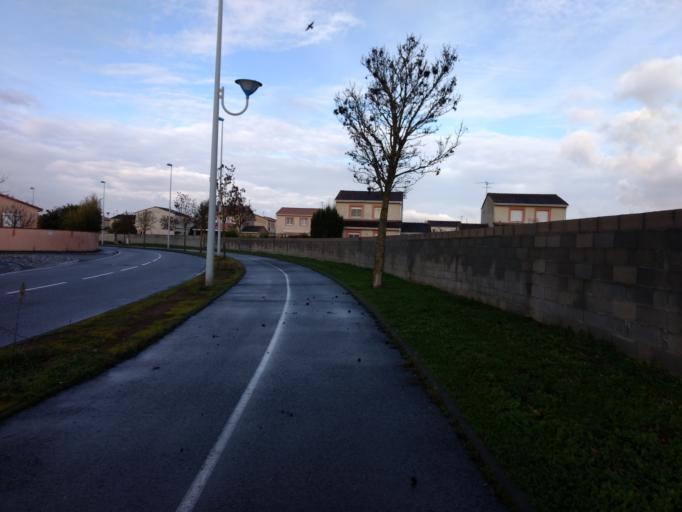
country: FR
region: Midi-Pyrenees
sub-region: Departement de la Haute-Garonne
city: Tournefeuille
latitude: 43.5958
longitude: 1.3231
